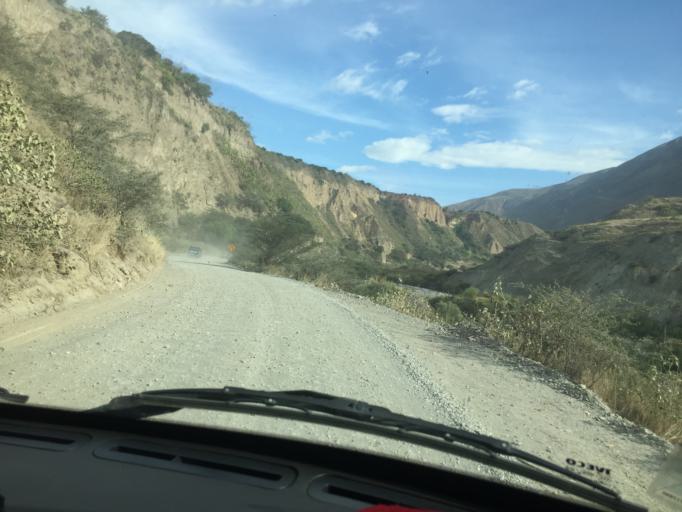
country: EC
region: Carchi
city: El Angel
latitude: 0.6018
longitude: -78.1384
